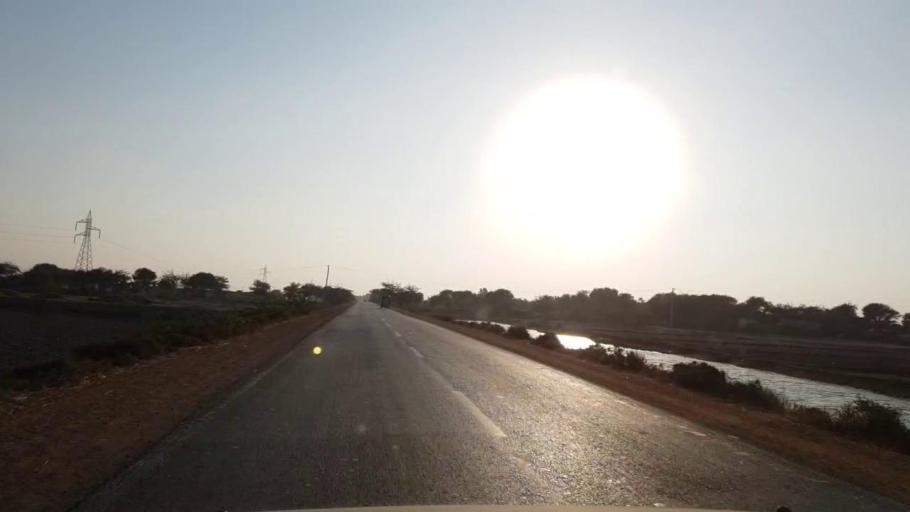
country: PK
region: Sindh
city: Daro Mehar
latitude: 24.6476
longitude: 68.1234
